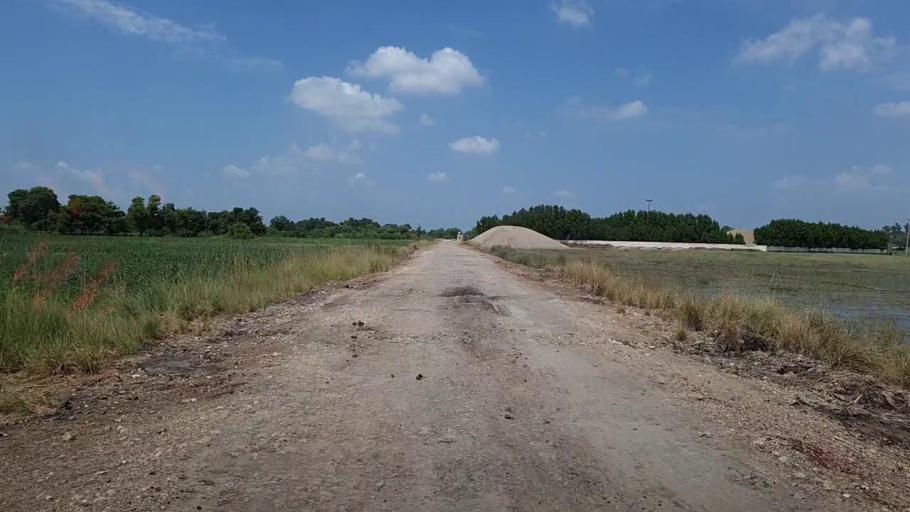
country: PK
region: Sindh
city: Bhiria
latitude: 26.9769
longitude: 68.2417
